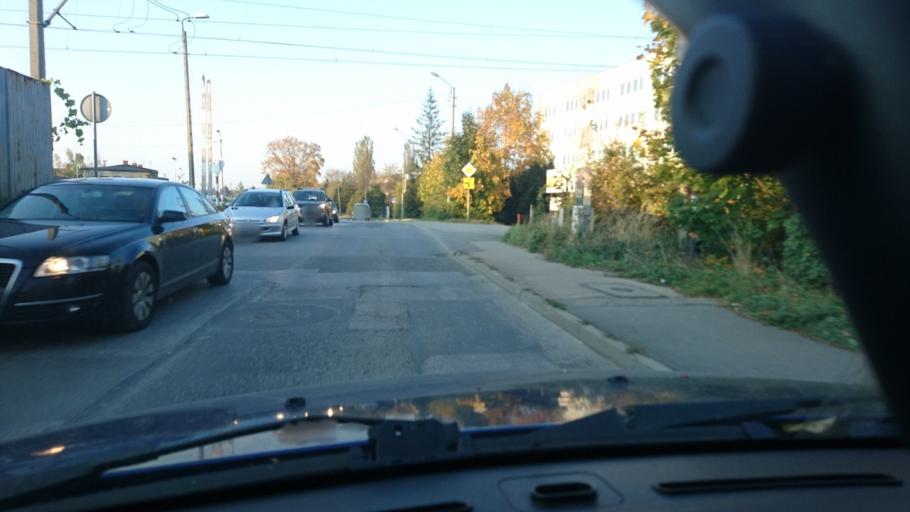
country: PL
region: Silesian Voivodeship
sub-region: Powiat bielski
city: Jaworze
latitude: 49.8106
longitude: 18.9843
